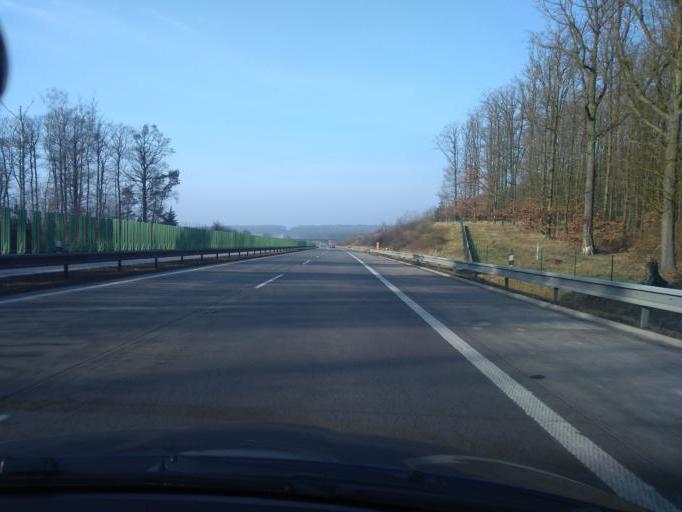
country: CZ
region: Pardubicky
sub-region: Okres Pardubice
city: Lazne Bohdanec
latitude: 50.1364
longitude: 15.6189
